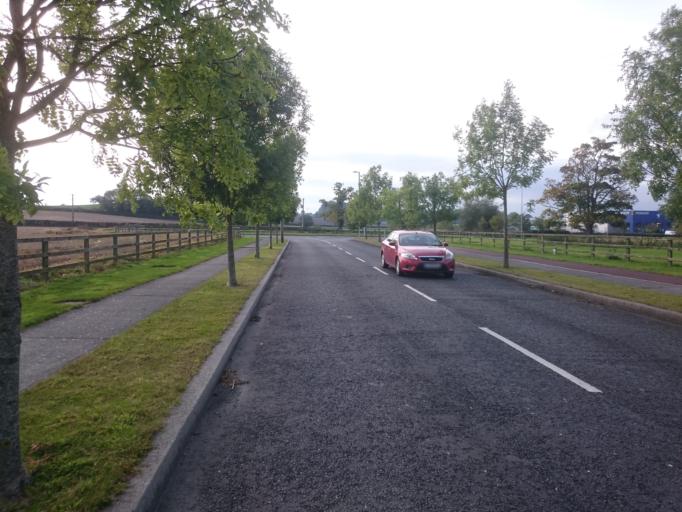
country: IE
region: Leinster
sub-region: Kilkenny
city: Kilkenny
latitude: 52.6323
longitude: -7.2478
